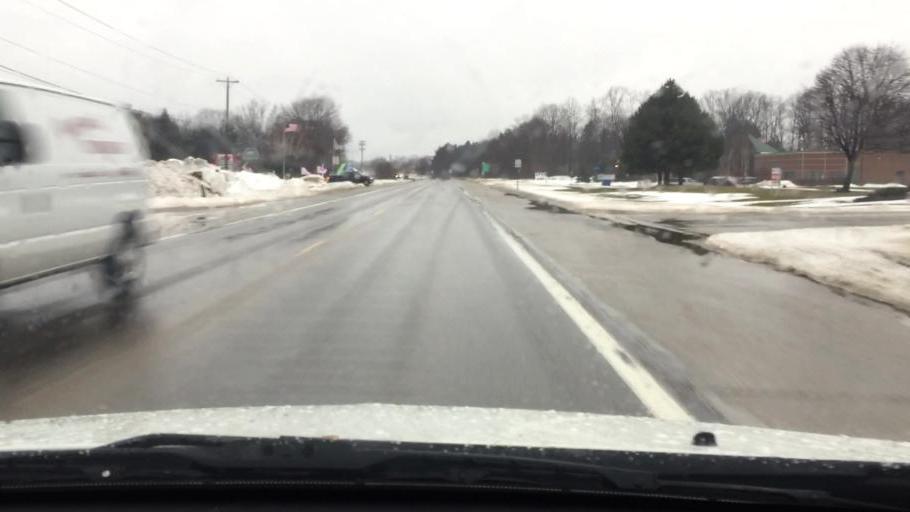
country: US
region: Michigan
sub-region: Charlevoix County
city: Charlevoix
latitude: 45.2986
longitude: -85.2557
